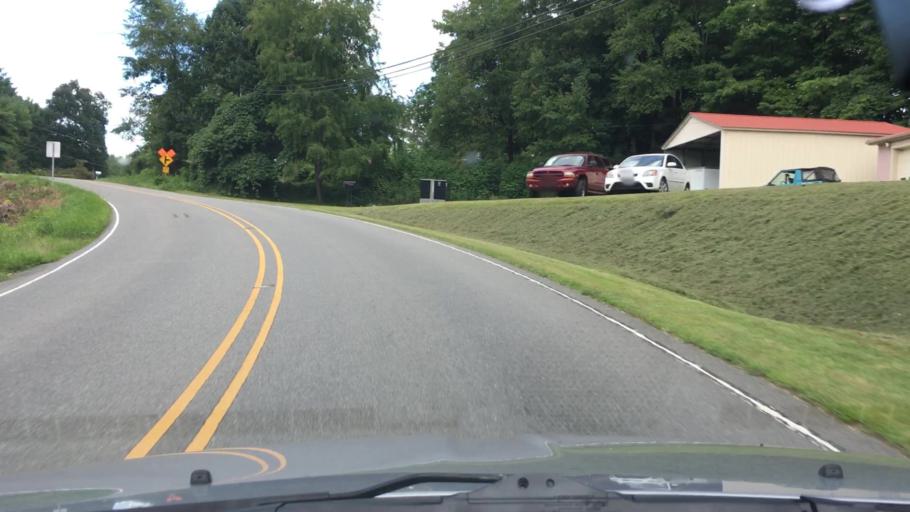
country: US
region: North Carolina
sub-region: Yancey County
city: Burnsville
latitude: 35.8375
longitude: -82.1884
